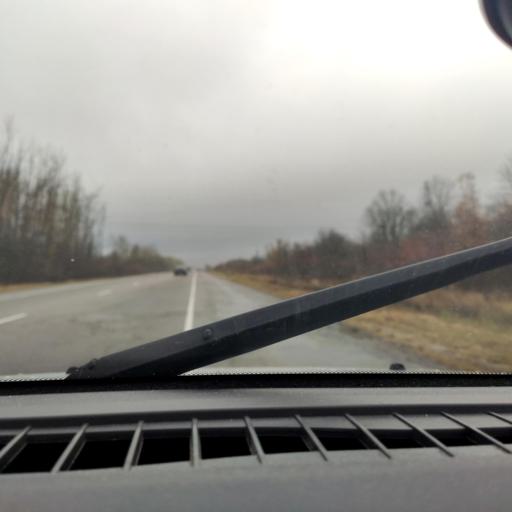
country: RU
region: Voronezj
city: Kolodeznyy
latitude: 51.2757
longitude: 39.0461
